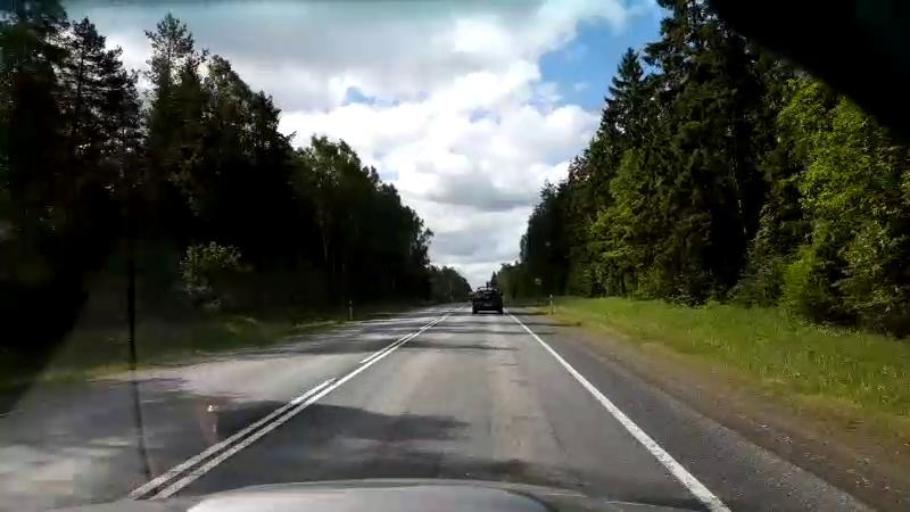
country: EE
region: Harju
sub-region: Saue linn
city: Saue
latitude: 59.2040
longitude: 24.4974
